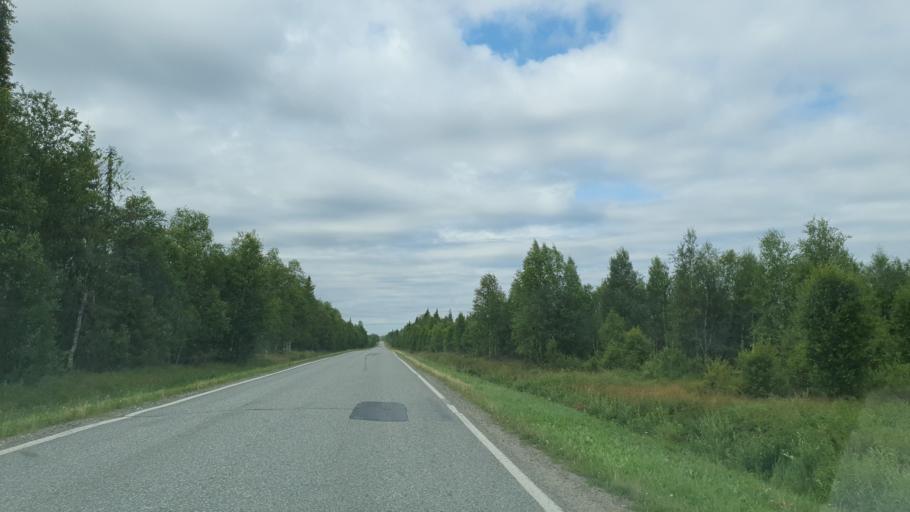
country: FI
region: Lapland
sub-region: Tunturi-Lappi
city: Kittilae
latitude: 67.6154
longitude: 25.3736
